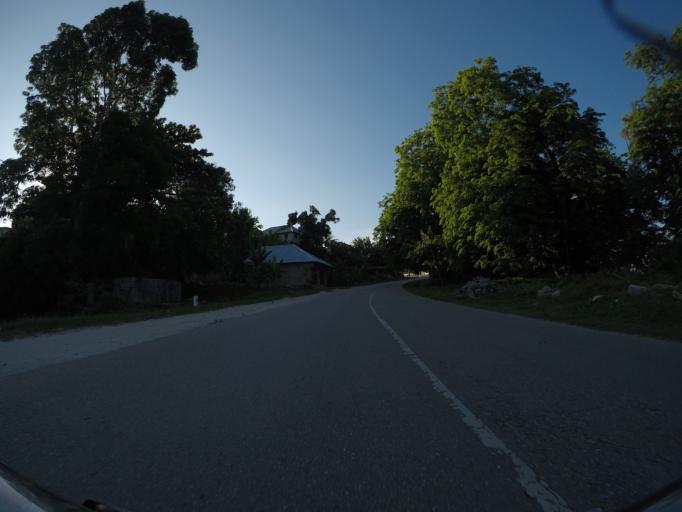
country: TZ
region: Pemba South
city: Uwelini
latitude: -5.3626
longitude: 39.6557
